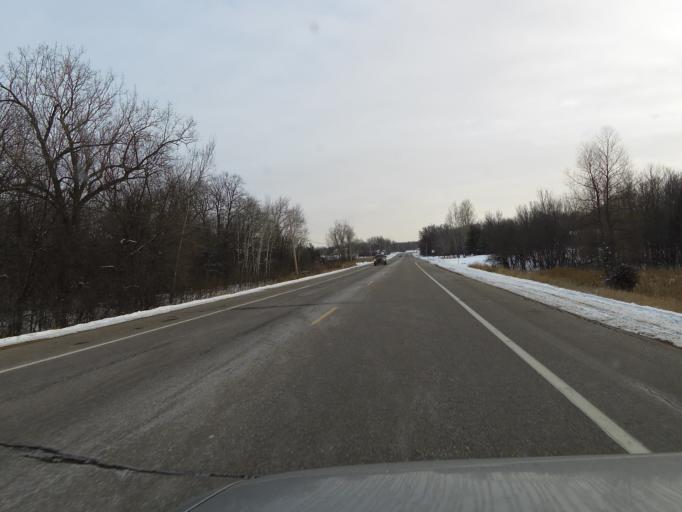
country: US
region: Minnesota
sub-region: Scott County
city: Shakopee
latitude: 44.7317
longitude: -93.4955
